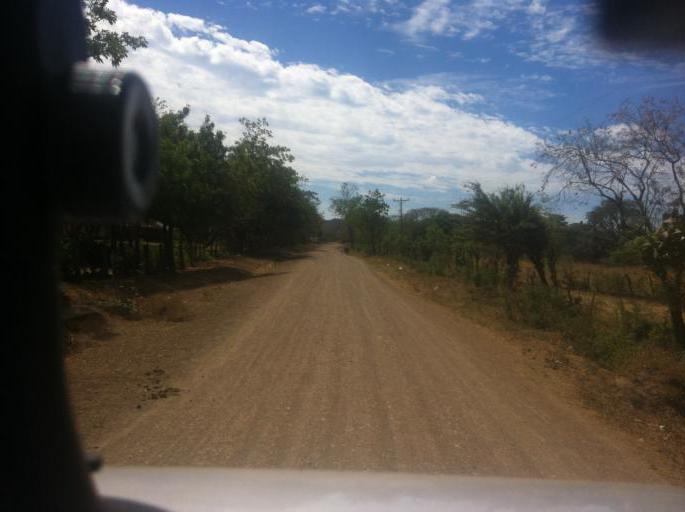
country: NI
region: Granada
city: Nandaime
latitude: 11.6216
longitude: -86.0255
